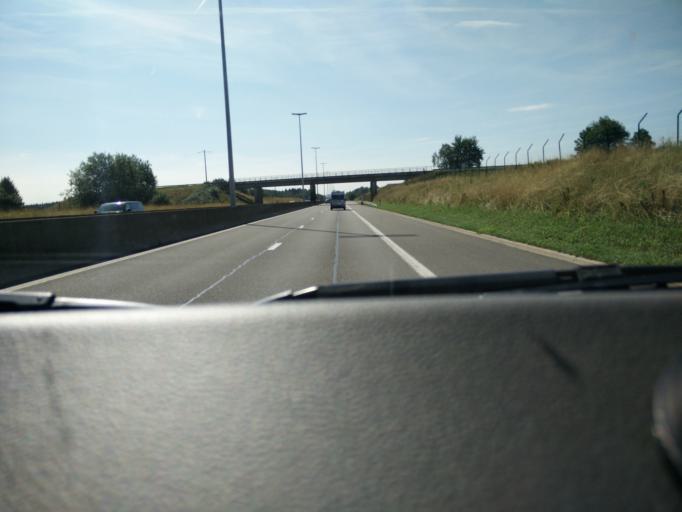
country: BE
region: Wallonia
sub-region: Province du Luxembourg
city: Leglise
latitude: 49.8346
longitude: 5.5119
